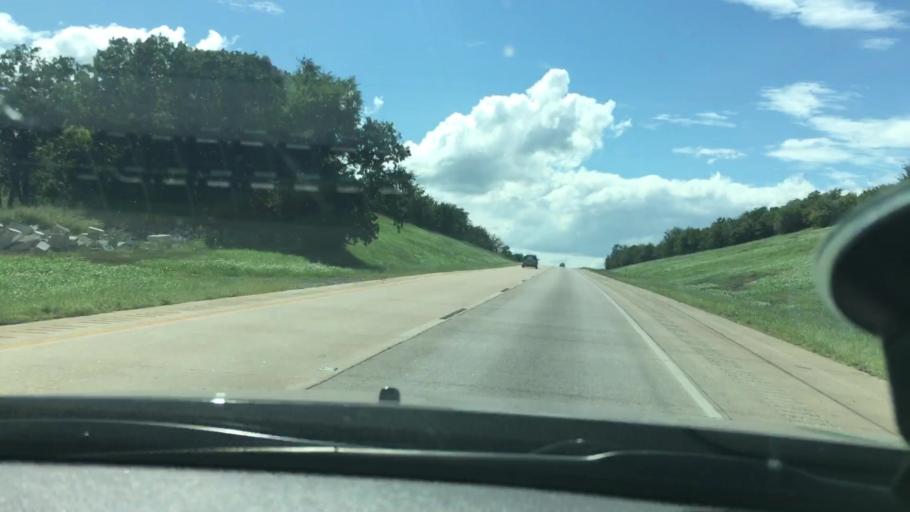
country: US
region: Oklahoma
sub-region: Sequoyah County
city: Vian
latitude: 35.4917
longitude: -95.0580
